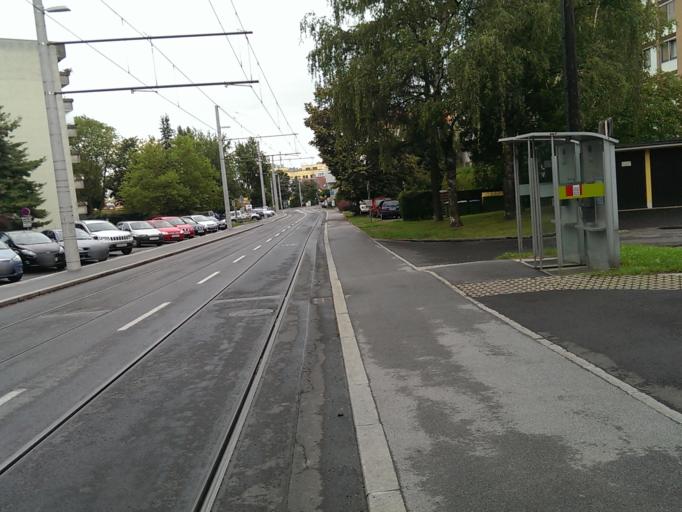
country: AT
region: Styria
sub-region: Graz Stadt
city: Graz
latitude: 47.0617
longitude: 15.4716
